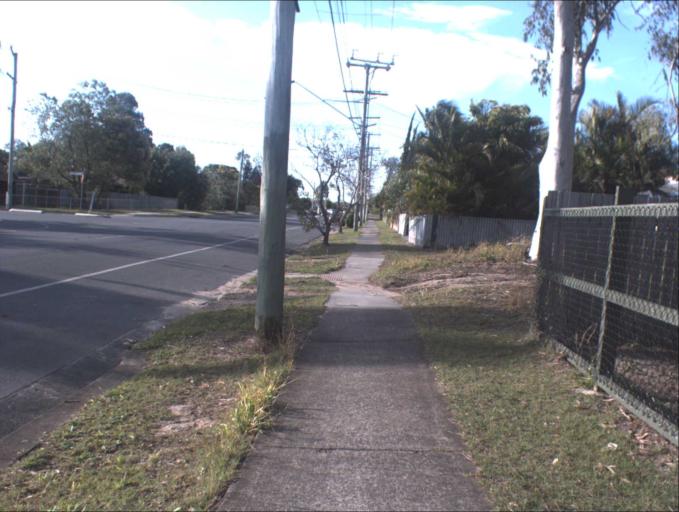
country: AU
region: Queensland
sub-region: Logan
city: Waterford West
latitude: -27.6772
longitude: 153.1008
